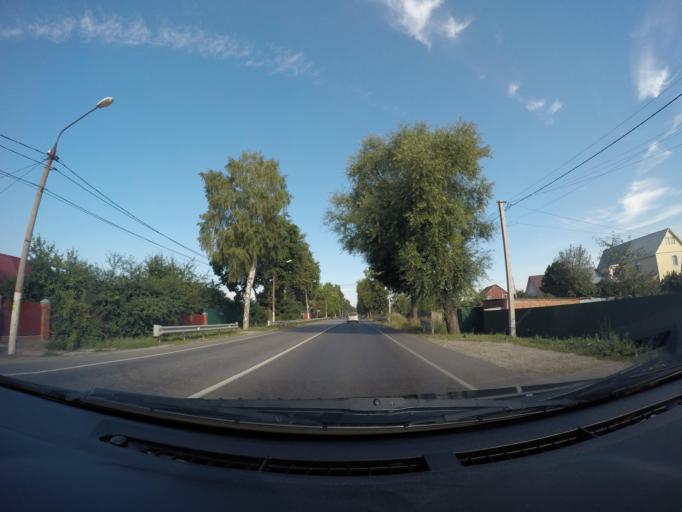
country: RU
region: Moskovskaya
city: Gzhel'
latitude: 55.6111
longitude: 38.3937
